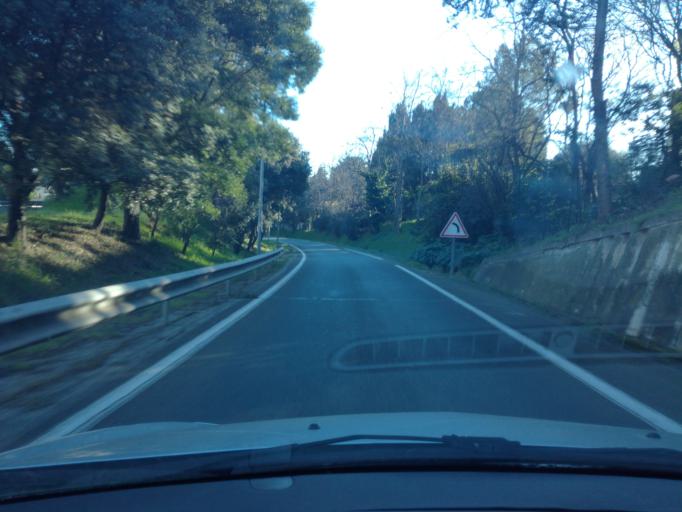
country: FR
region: Provence-Alpes-Cote d'Azur
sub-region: Departement des Alpes-Maritimes
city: Antibes
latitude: 43.5799
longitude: 7.1139
